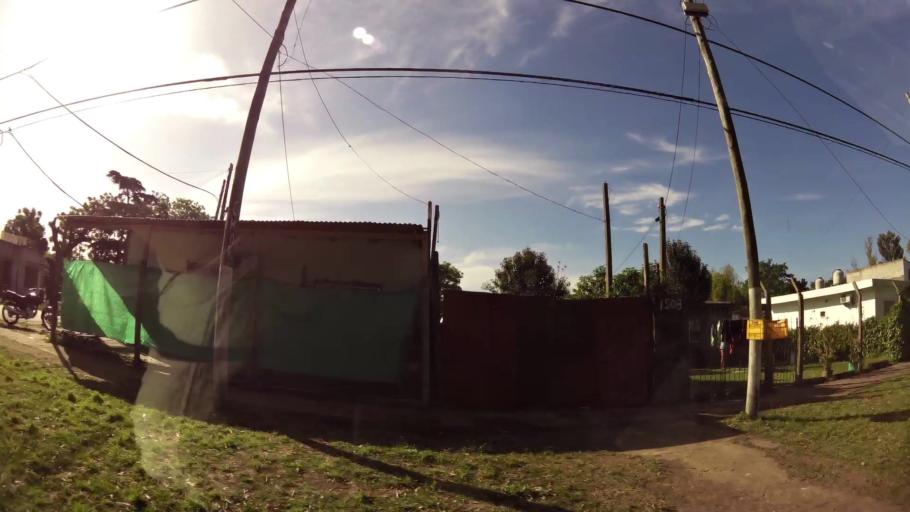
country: AR
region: Buenos Aires
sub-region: Partido de Quilmes
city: Quilmes
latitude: -34.7893
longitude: -58.2350
